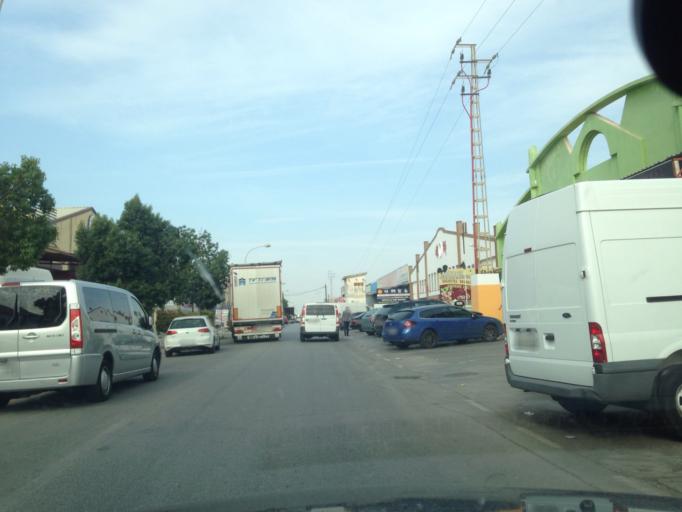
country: ES
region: Andalusia
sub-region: Provincia de Malaga
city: Malaga
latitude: 36.6897
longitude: -4.4745
